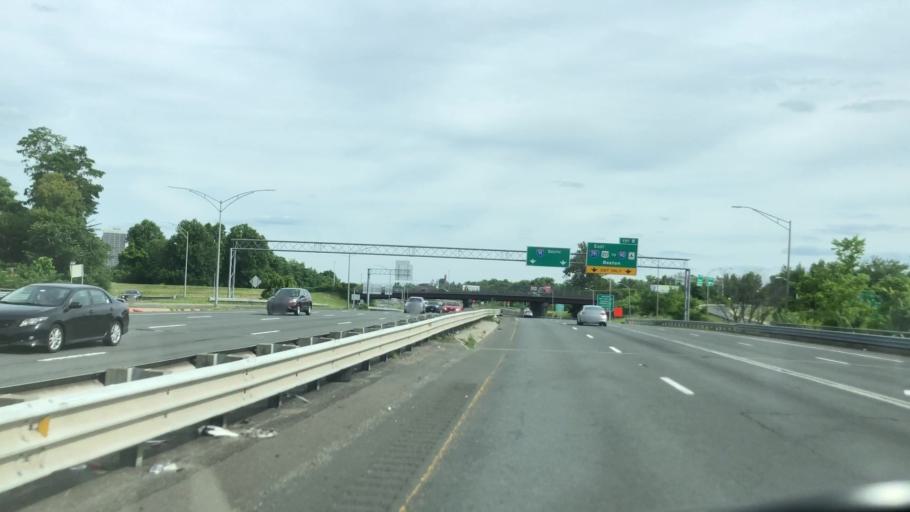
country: US
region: Massachusetts
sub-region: Hampden County
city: West Springfield
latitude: 42.1139
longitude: -72.6079
